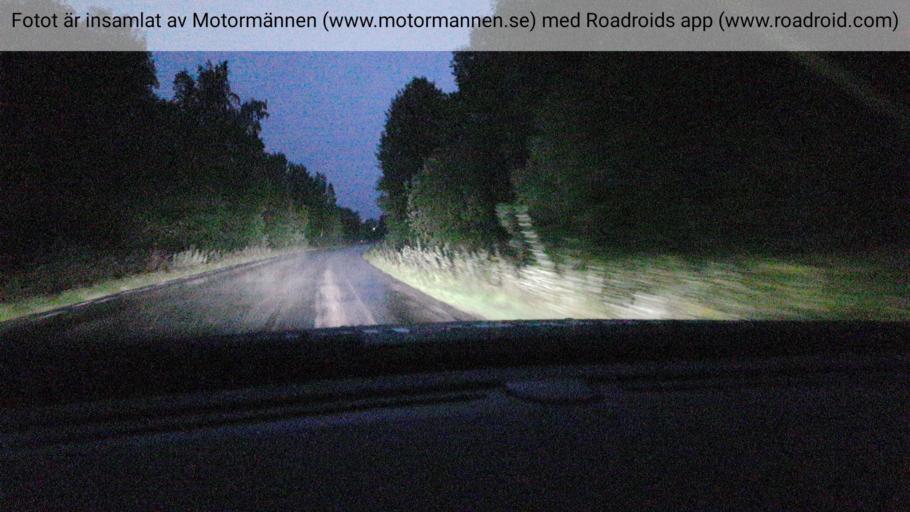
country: SE
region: Vaestra Goetaland
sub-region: Falkopings Kommun
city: Akarp
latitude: 58.2642
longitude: 13.7418
